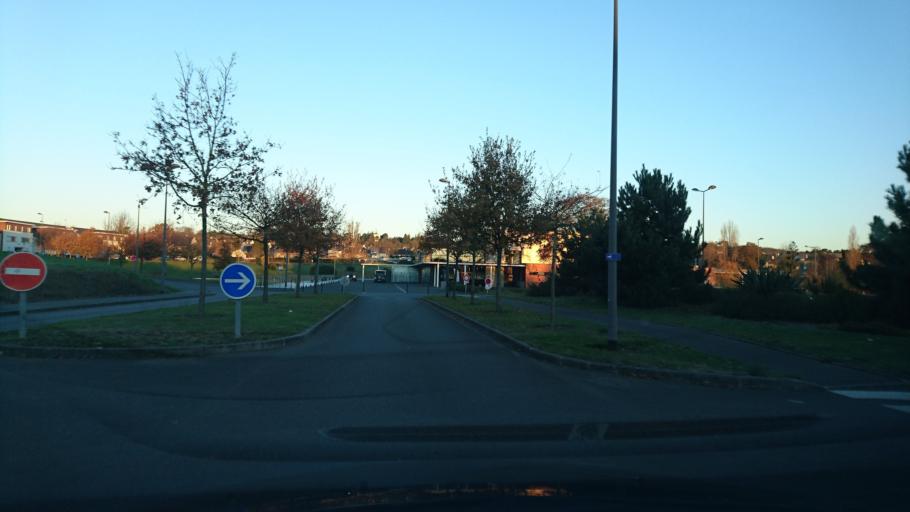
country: FR
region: Brittany
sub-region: Departement des Cotes-d'Armor
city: Pledran
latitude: 48.4470
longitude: -2.7431
